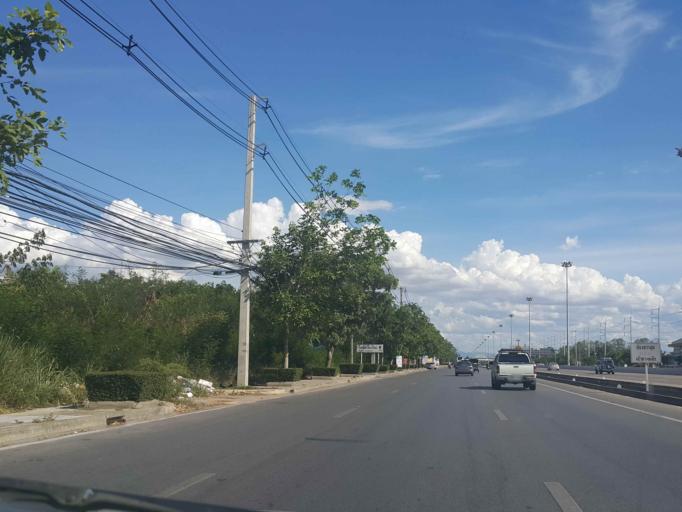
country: TH
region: Chiang Mai
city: Chiang Mai
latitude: 18.7758
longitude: 99.0281
